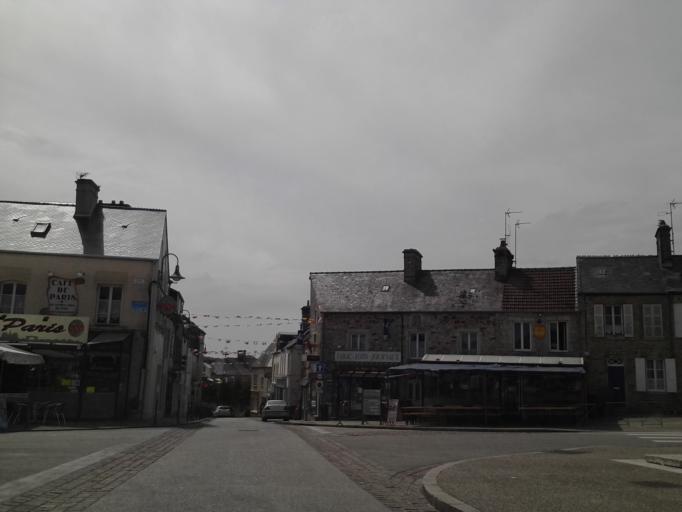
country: FR
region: Lower Normandy
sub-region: Departement de la Manche
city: Bricquebec
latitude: 49.4713
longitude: -1.6322
